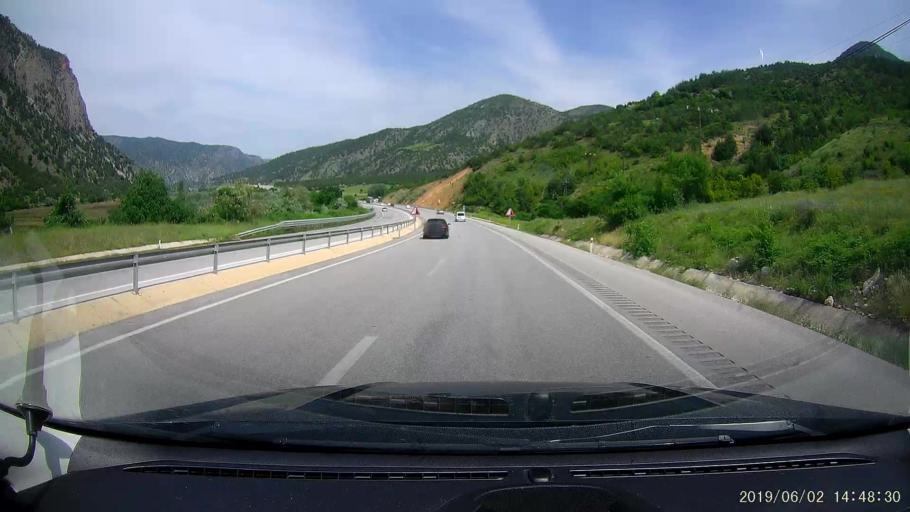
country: TR
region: Corum
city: Hacihamza
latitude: 41.0623
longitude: 34.4812
